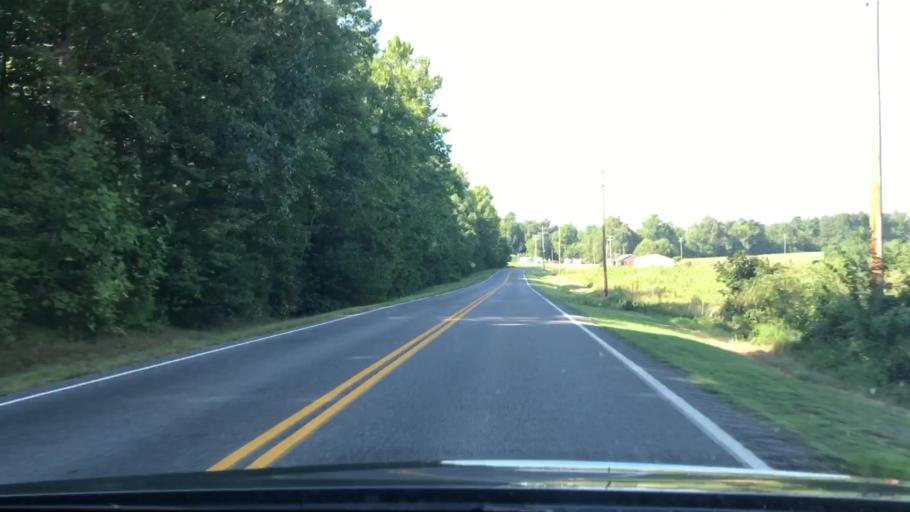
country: US
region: Kentucky
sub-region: Marshall County
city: Benton
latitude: 36.7767
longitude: -88.4785
